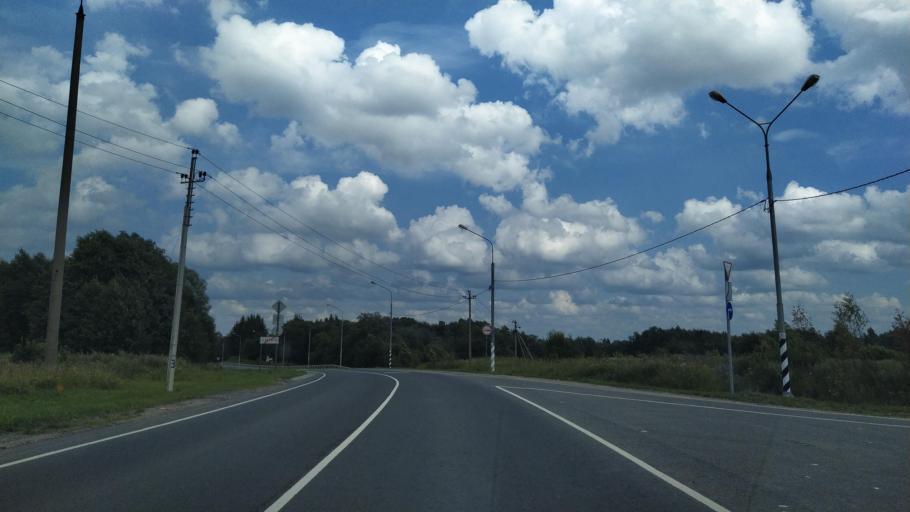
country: RU
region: Pskov
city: Dno
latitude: 58.0589
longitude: 29.9737
